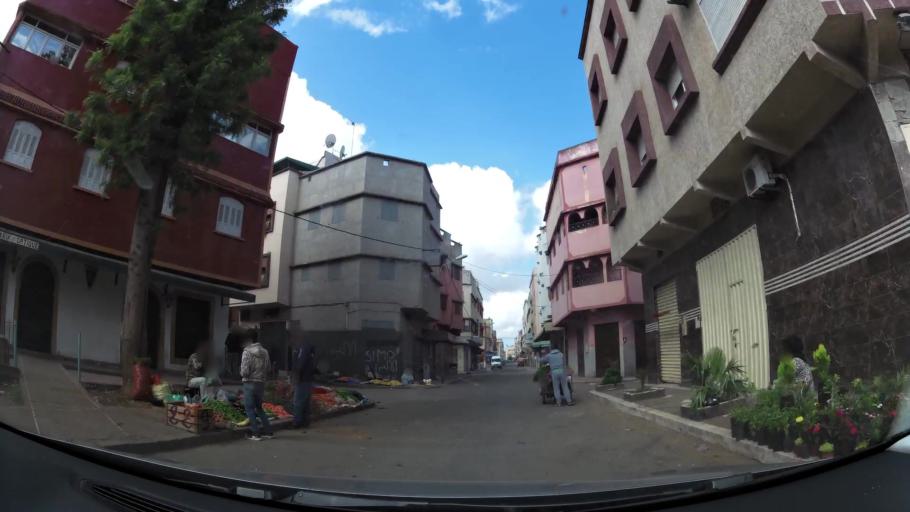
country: MA
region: Gharb-Chrarda-Beni Hssen
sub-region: Kenitra Province
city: Kenitra
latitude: 34.2619
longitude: -6.5641
